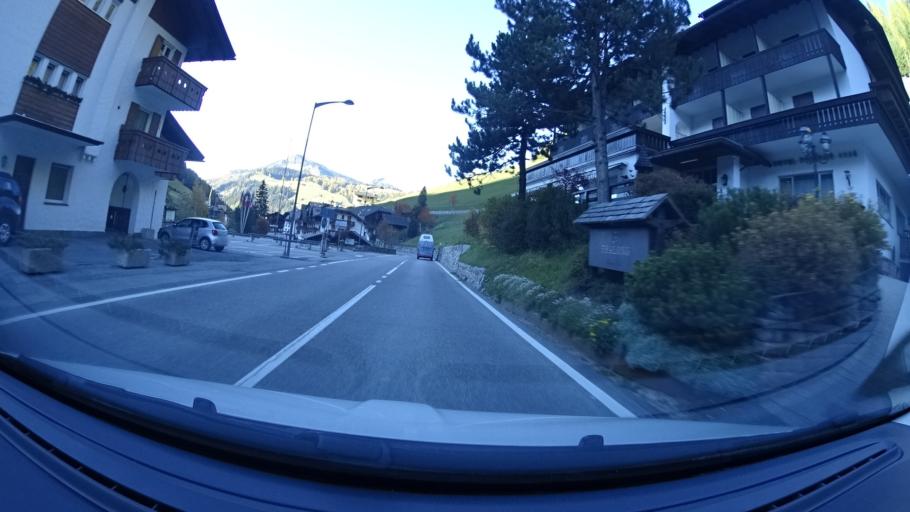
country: IT
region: Trentino-Alto Adige
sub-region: Bolzano
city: Selva
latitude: 46.5493
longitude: 11.7664
